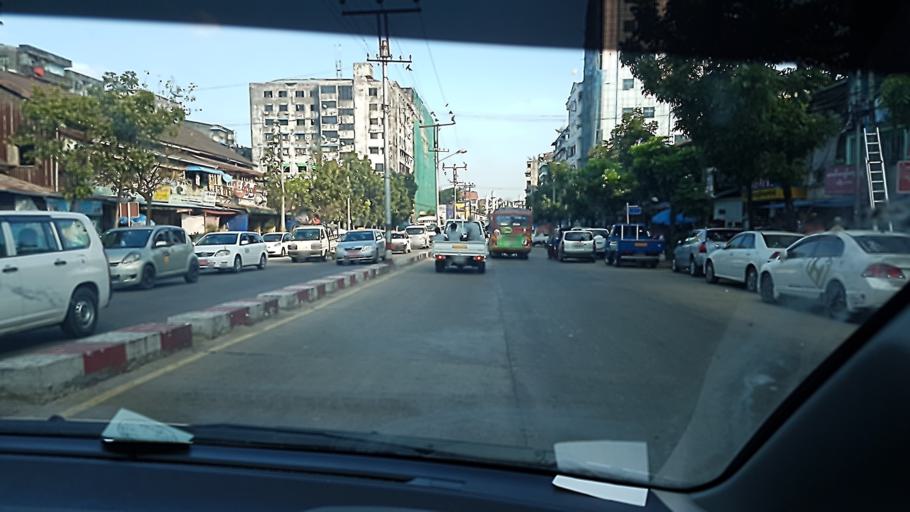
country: MM
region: Yangon
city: Yangon
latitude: 16.8110
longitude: 96.1736
